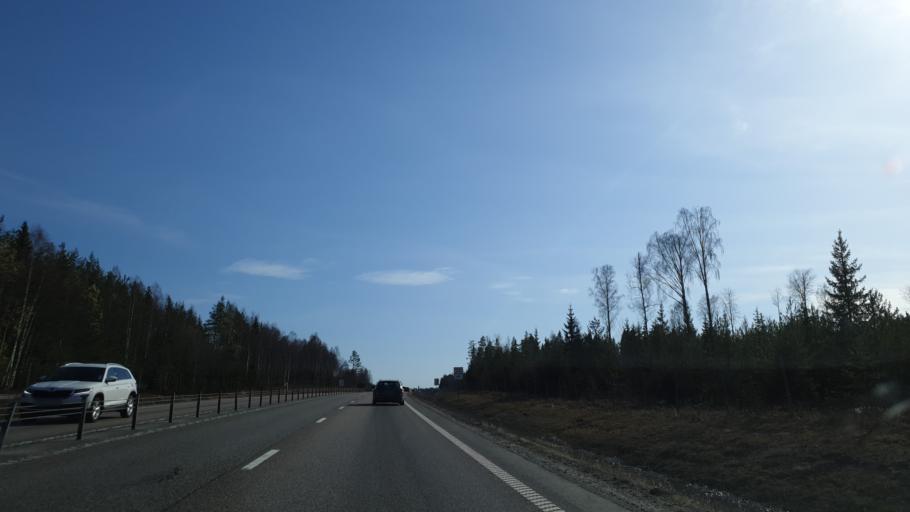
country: SE
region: Vaesternorrland
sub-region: Sundsvalls Kommun
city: Njurundabommen
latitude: 62.2089
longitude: 17.3736
